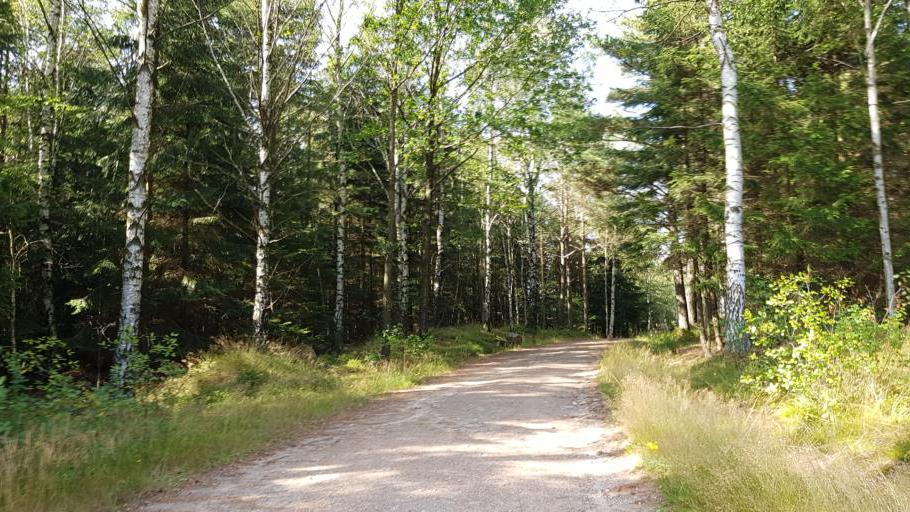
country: SE
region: Vaestra Goetaland
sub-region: Harryda Kommun
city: Molnlycke
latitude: 57.6778
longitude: 12.0698
